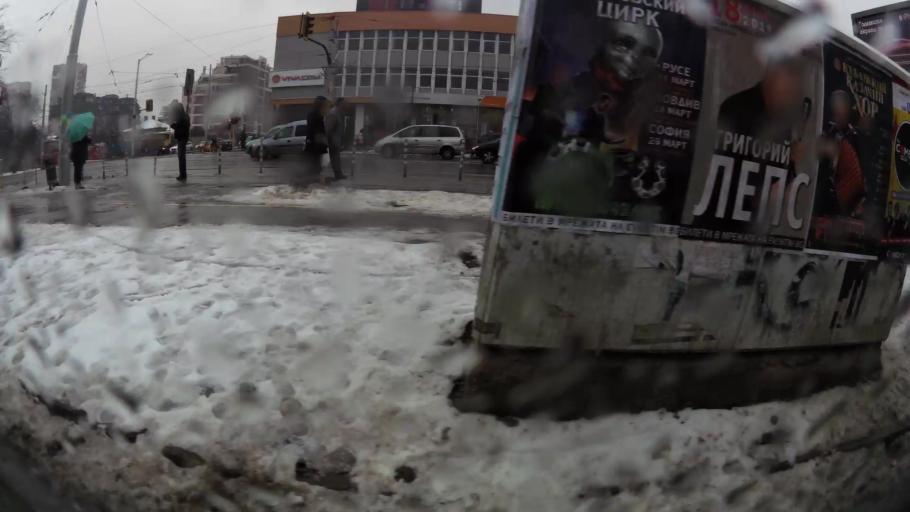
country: BG
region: Sofia-Capital
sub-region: Stolichna Obshtina
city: Sofia
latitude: 42.6717
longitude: 23.2721
